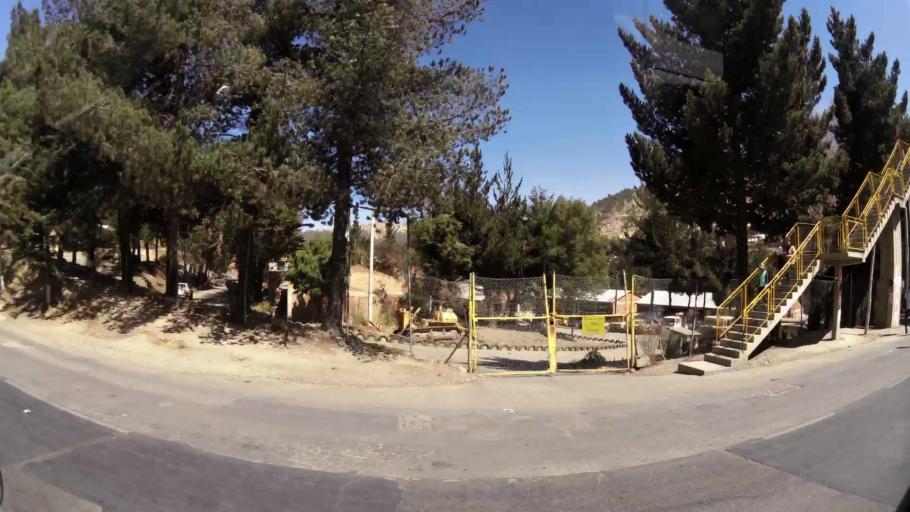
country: BO
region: La Paz
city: La Paz
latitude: -16.4602
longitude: -68.1472
